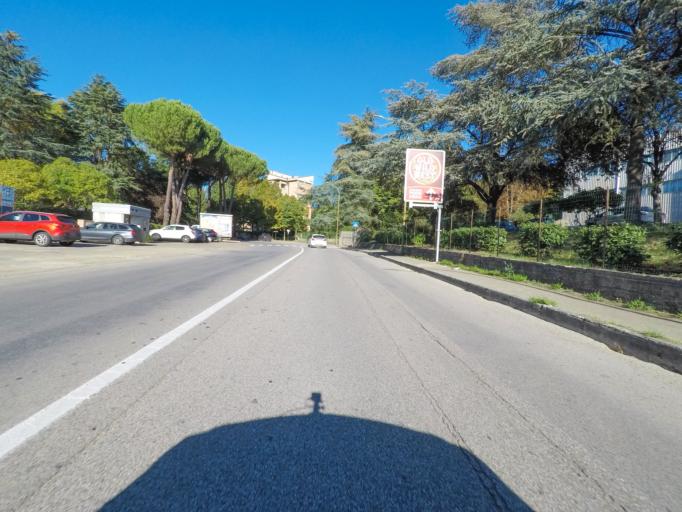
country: IT
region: Tuscany
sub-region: Provincia di Siena
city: Belverde
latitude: 43.3383
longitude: 11.2997
